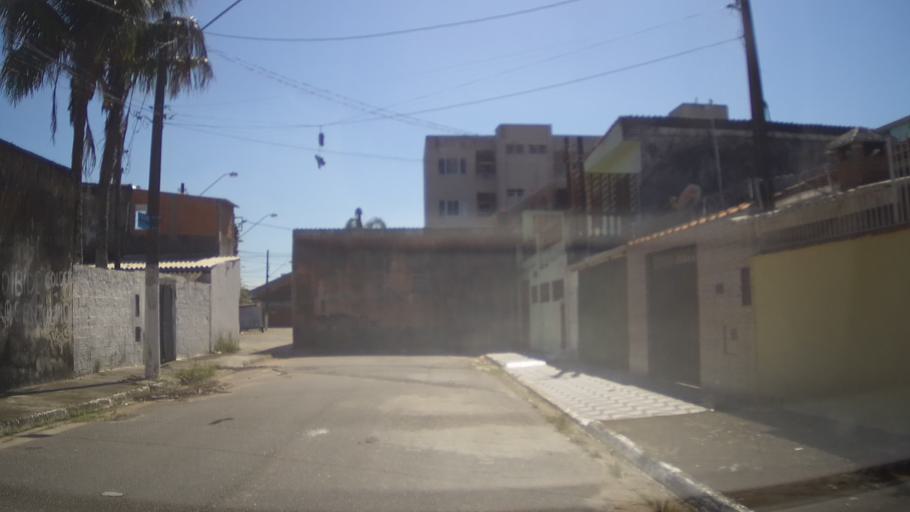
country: BR
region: Sao Paulo
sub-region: Praia Grande
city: Praia Grande
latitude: -24.0277
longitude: -46.4879
